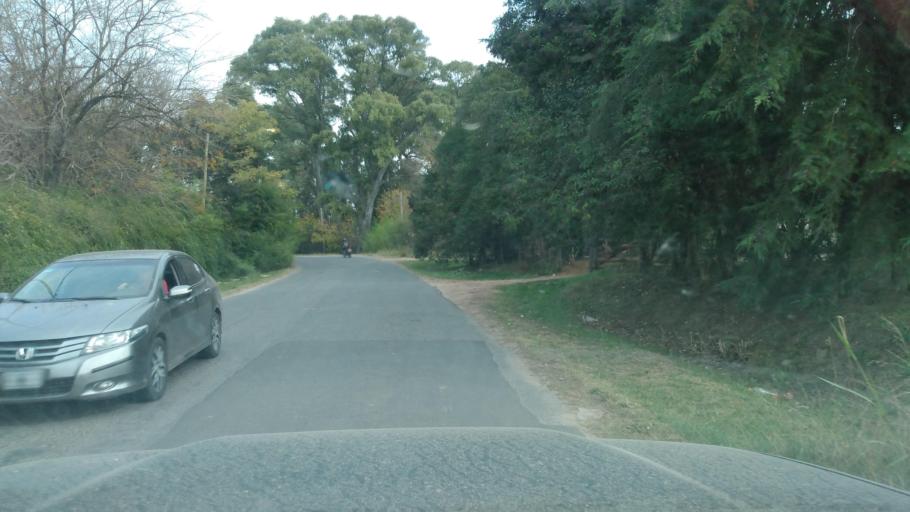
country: AR
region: Buenos Aires
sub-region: Partido de Lujan
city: Lujan
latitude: -34.5843
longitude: -59.1277
